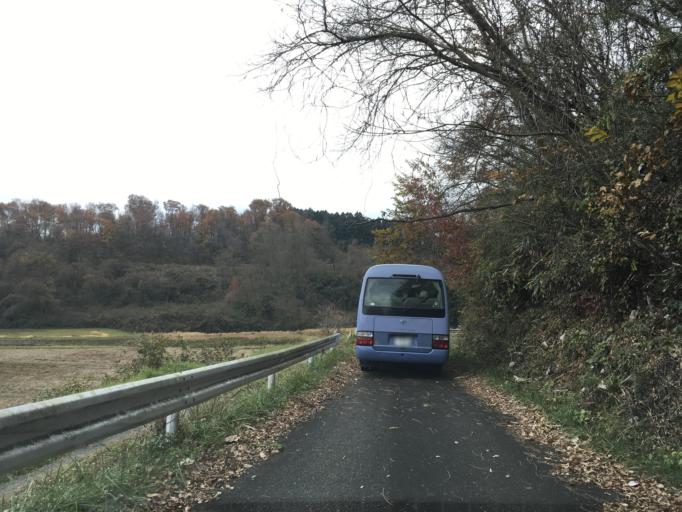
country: JP
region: Iwate
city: Ichinoseki
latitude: 38.8464
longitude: 141.0348
